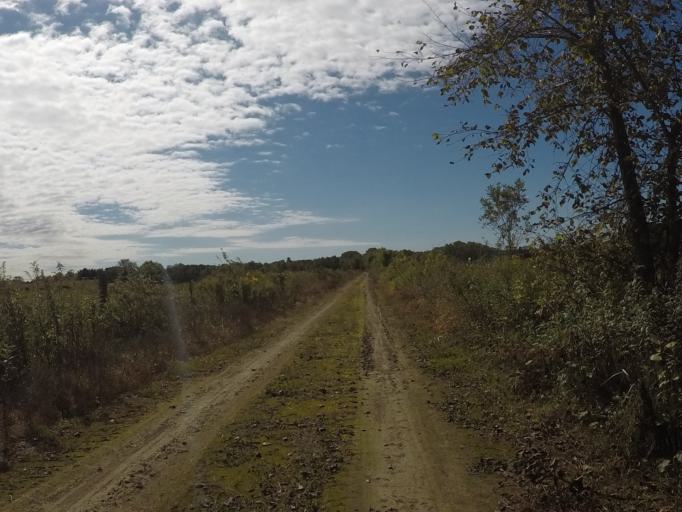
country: US
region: Wisconsin
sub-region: Richland County
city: Richland Center
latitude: 43.2340
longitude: -90.2999
